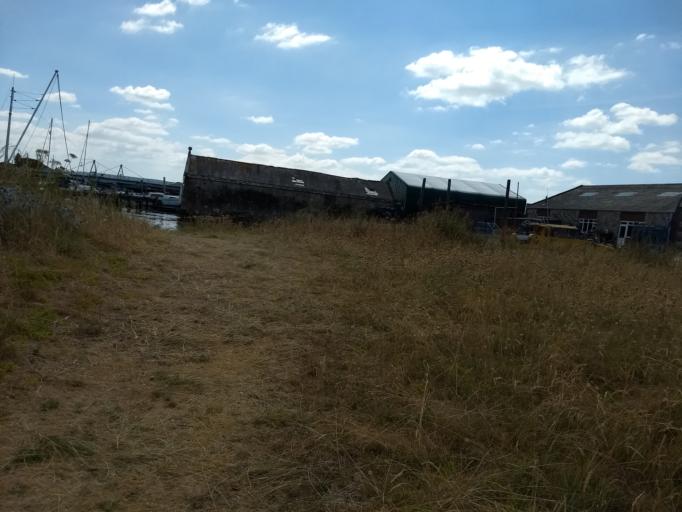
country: GB
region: England
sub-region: Isle of Wight
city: Yarmouth
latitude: 50.7052
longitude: -1.5057
